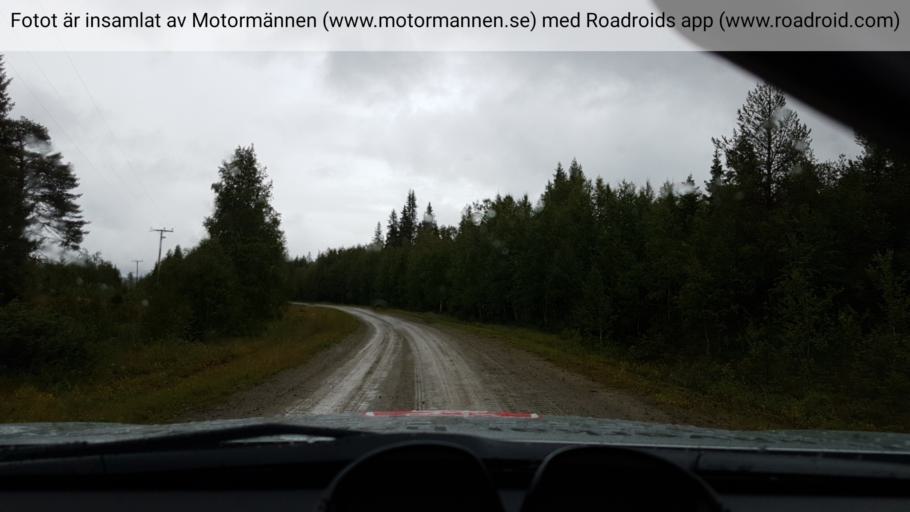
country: SE
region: Vaesterbotten
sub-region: Asele Kommun
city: Insjon
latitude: 64.7850
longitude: 17.5470
